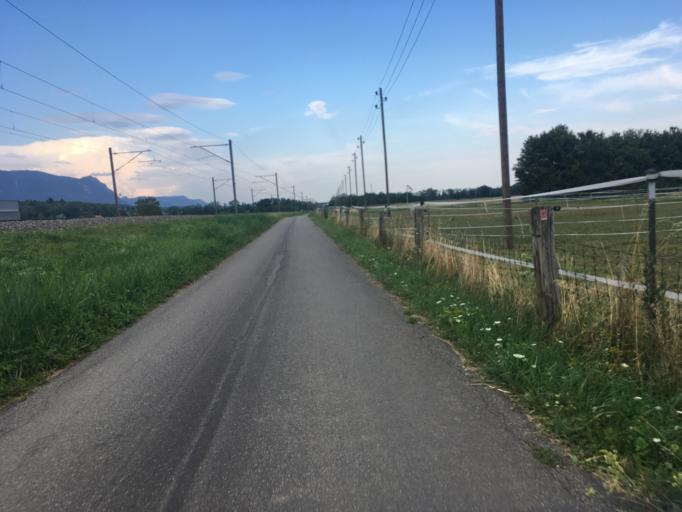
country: CH
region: Solothurn
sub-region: Bezirk Lebern
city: Bettlach
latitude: 47.1956
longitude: 7.4322
